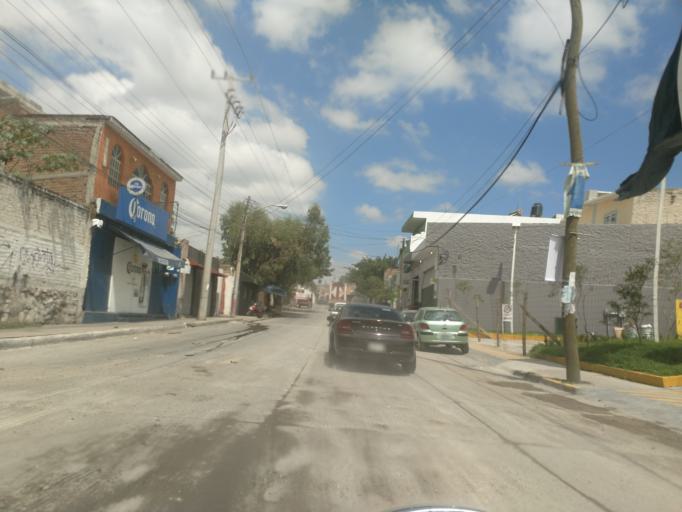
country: MX
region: Jalisco
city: Tlaquepaque
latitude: 20.6461
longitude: -103.2731
